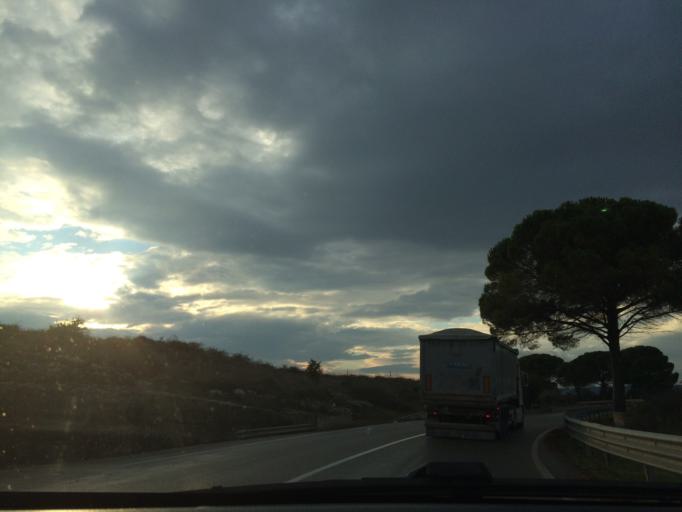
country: IT
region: Basilicate
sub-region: Provincia di Matera
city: Matera
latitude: 40.6770
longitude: 16.6422
